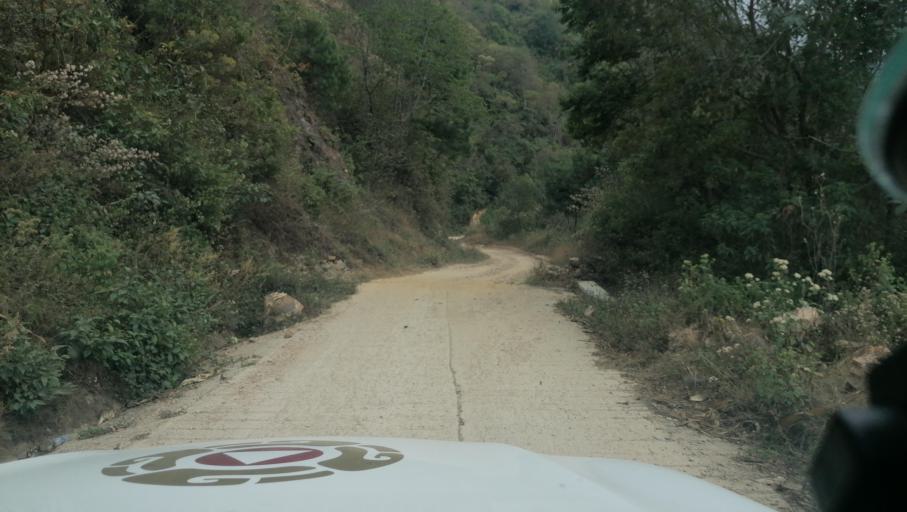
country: GT
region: San Marcos
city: Tacana
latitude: 15.2191
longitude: -92.1996
